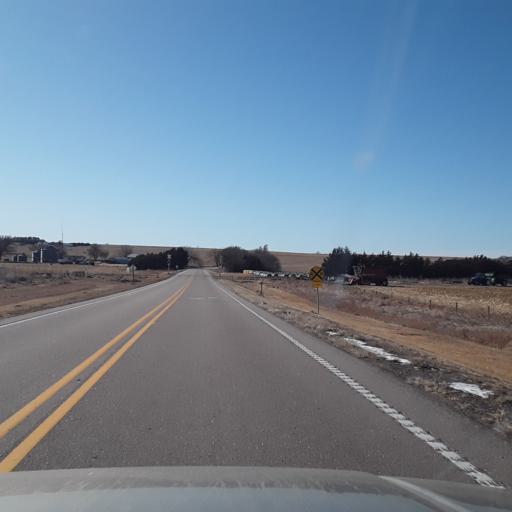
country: US
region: Nebraska
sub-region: Frontier County
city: Stockville
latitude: 40.7039
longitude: -100.2492
